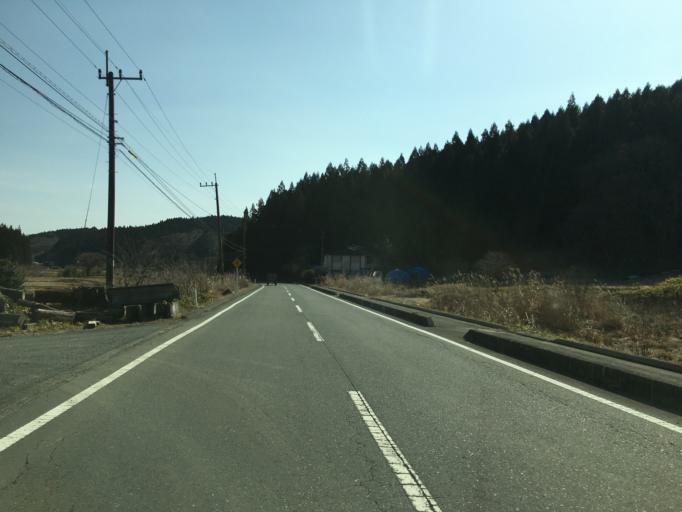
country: JP
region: Ibaraki
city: Takahagi
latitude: 36.8007
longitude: 140.5778
